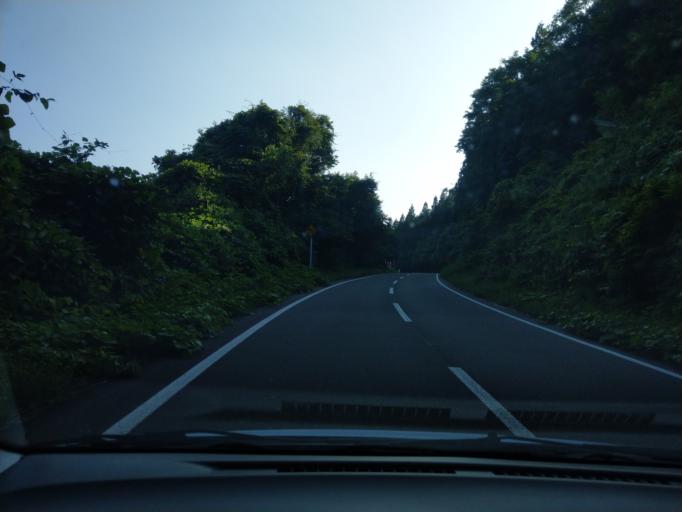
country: JP
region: Akita
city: Akita
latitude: 39.5763
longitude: 140.2340
